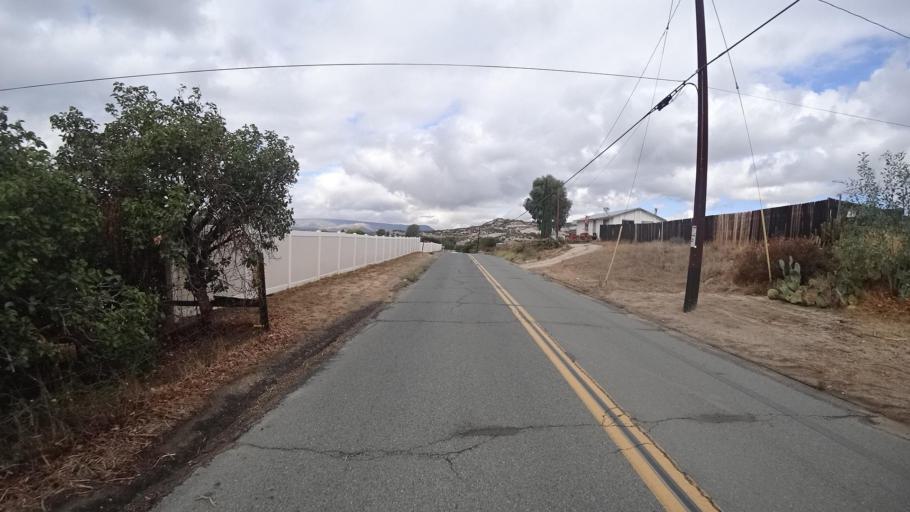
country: US
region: California
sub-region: San Diego County
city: Campo
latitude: 32.6305
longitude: -116.4290
